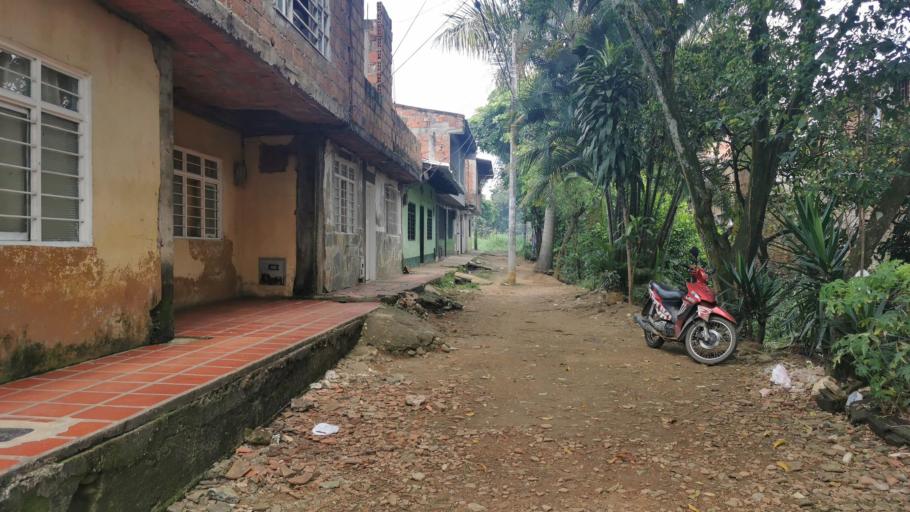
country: CO
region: Valle del Cauca
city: Jamundi
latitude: 3.2662
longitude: -76.5391
